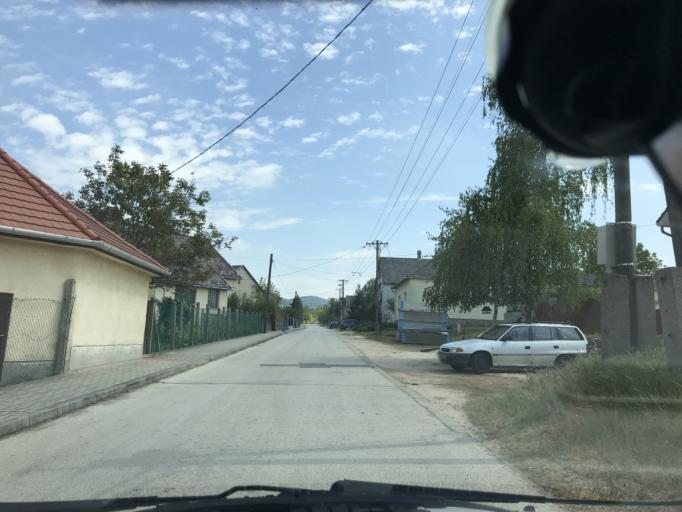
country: HU
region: Komarom-Esztergom
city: Piliscsev
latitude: 47.6711
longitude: 18.8128
